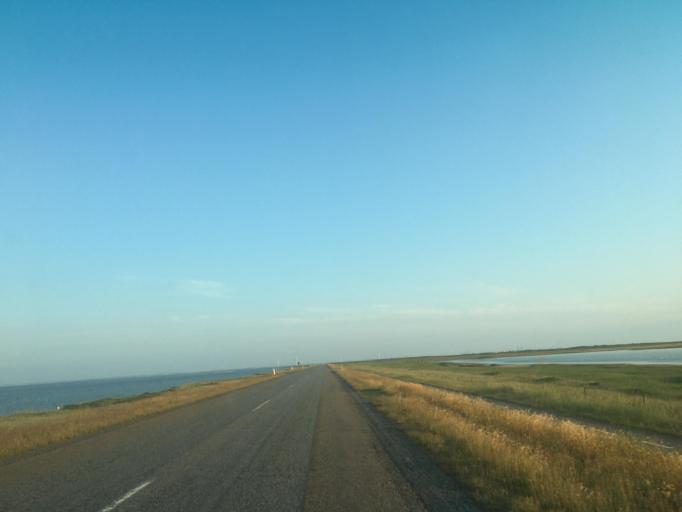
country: DK
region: Central Jutland
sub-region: Lemvig Kommune
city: Thyboron
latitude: 56.7415
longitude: 8.2505
